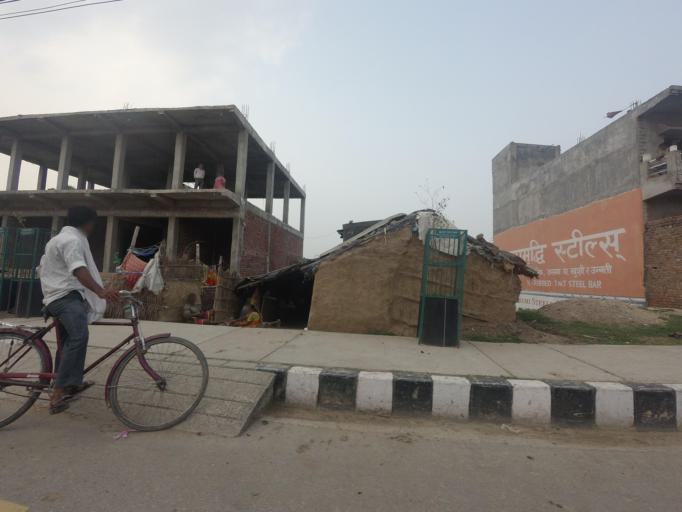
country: NP
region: Western Region
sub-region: Lumbini Zone
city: Bhairahawa
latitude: 27.5081
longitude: 83.4253
